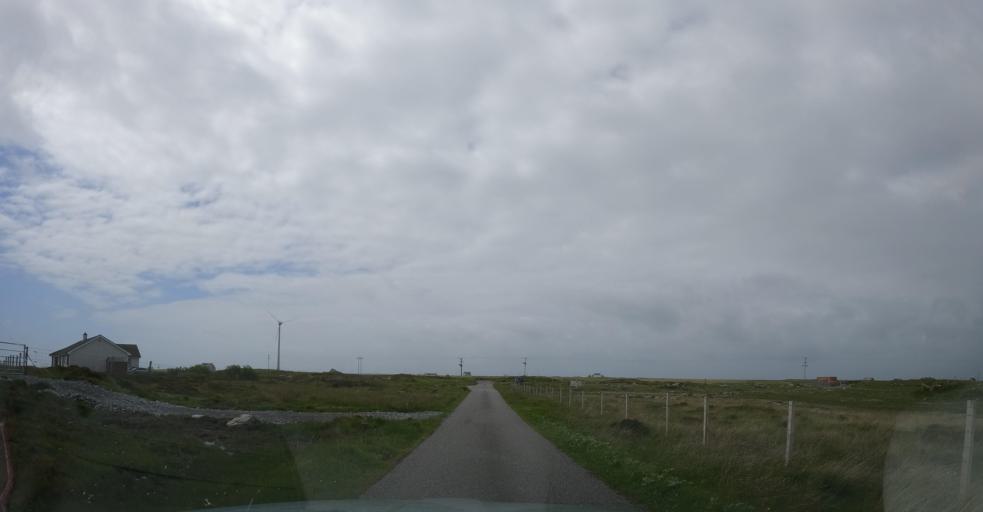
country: GB
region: Scotland
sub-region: Eilean Siar
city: Isle of South Uist
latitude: 57.2416
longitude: -7.3990
